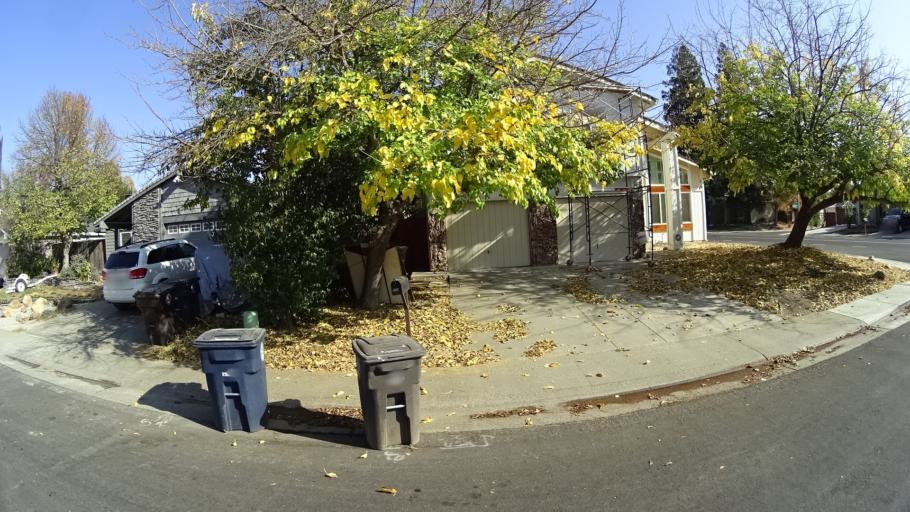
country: US
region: California
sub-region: Sacramento County
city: Citrus Heights
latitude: 38.6884
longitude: -121.2683
